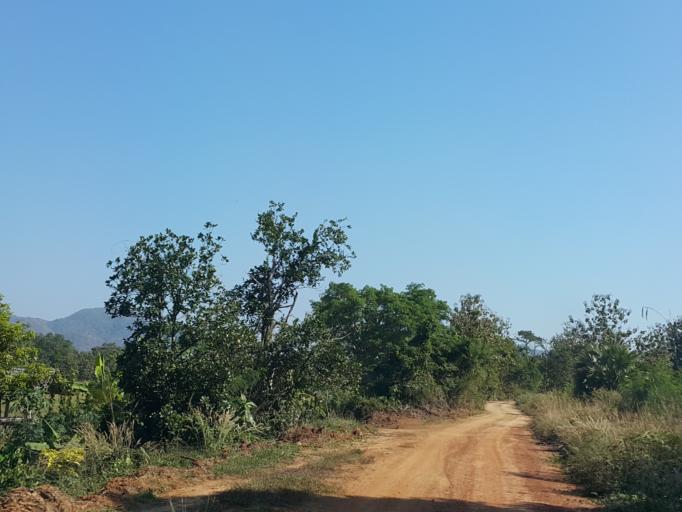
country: TH
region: Sukhothai
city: Thung Saliam
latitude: 17.3209
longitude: 99.4528
